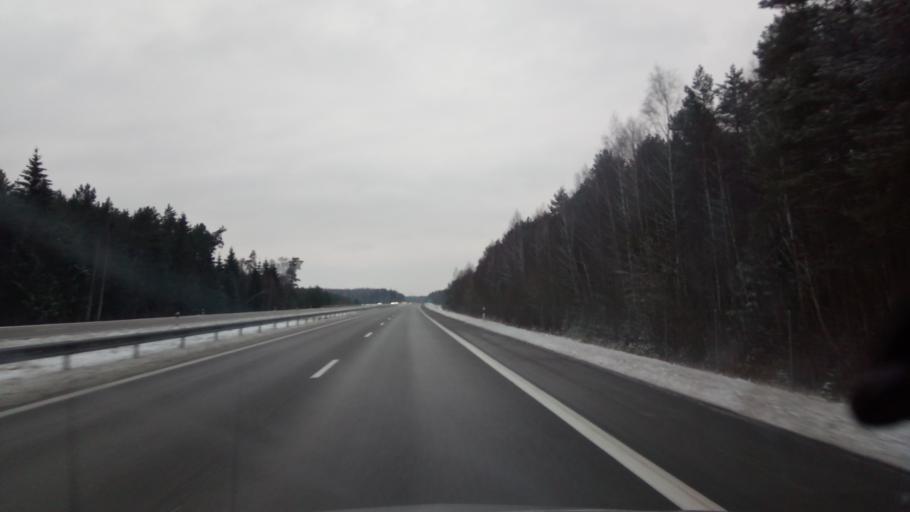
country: LT
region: Vilnius County
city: Ukmerge
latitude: 55.4922
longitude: 24.6266
